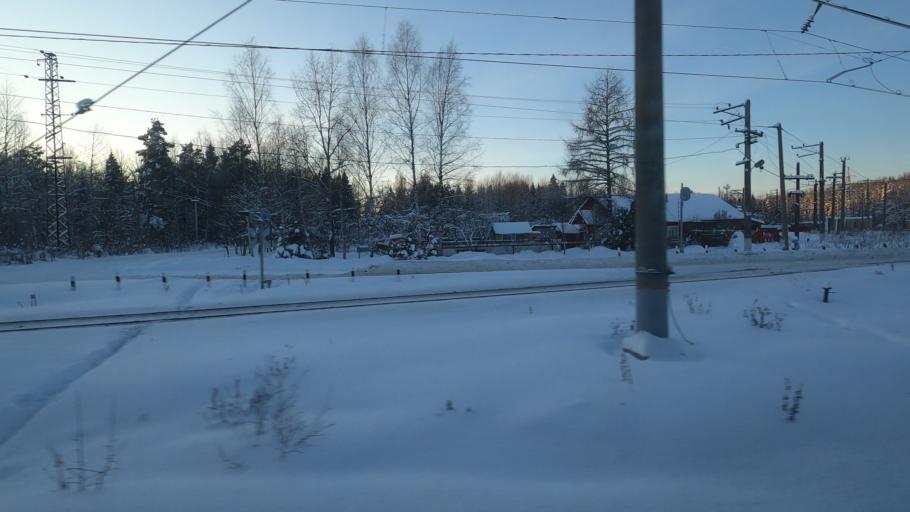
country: RU
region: Moskovskaya
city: Novo-Nikol'skoye
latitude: 56.5432
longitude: 37.5599
